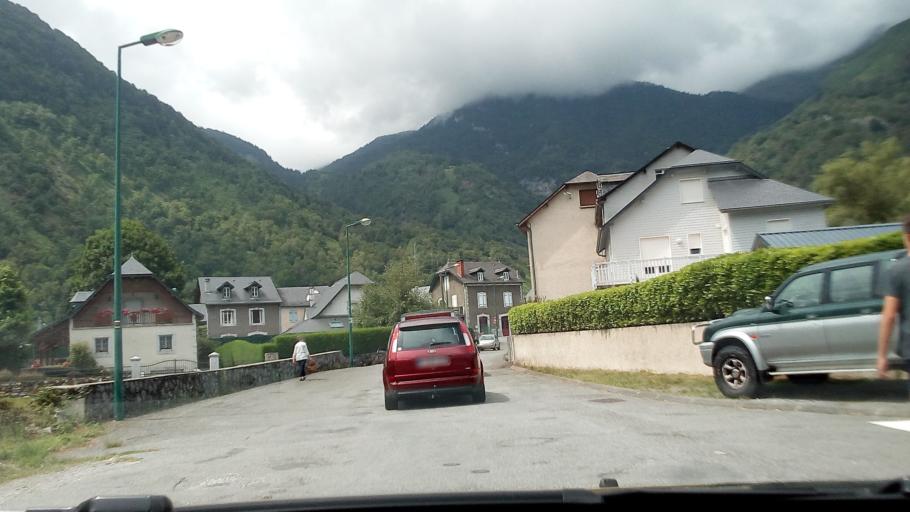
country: FR
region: Aquitaine
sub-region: Departement des Pyrenees-Atlantiques
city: Laruns
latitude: 42.9858
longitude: -0.4225
